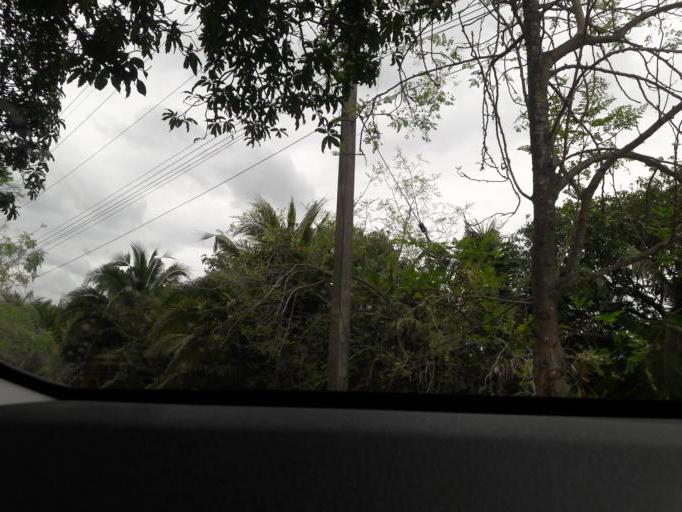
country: TH
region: Ratchaburi
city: Damnoen Saduak
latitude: 13.5663
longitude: 99.9854
